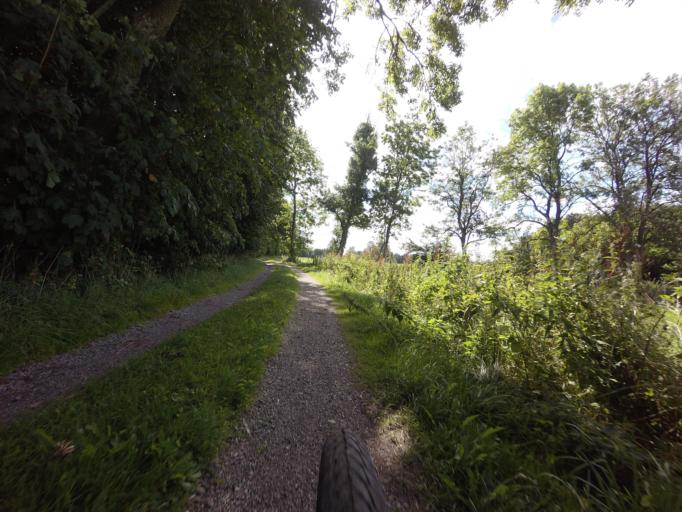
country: DK
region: Central Jutland
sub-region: Norddjurs Kommune
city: Auning
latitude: 56.4384
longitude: 10.3491
